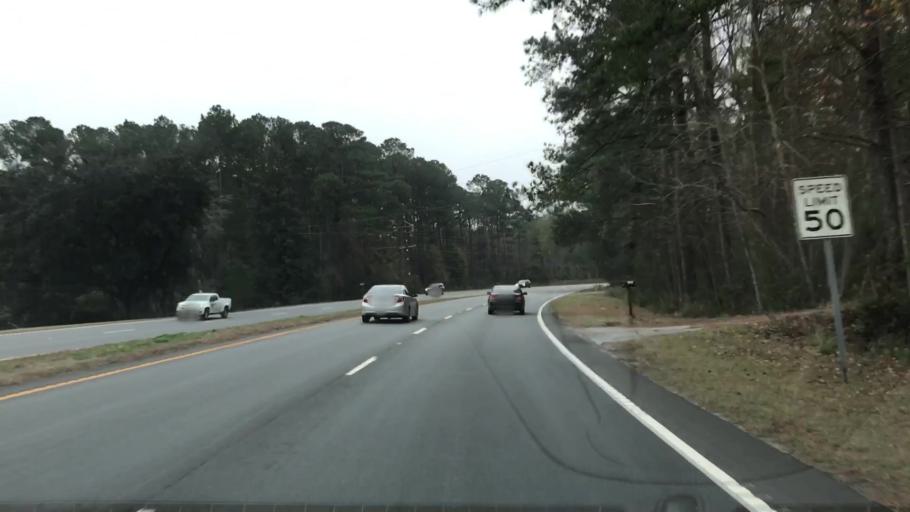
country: US
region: South Carolina
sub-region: Beaufort County
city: Laurel Bay
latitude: 32.5854
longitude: -80.7436
